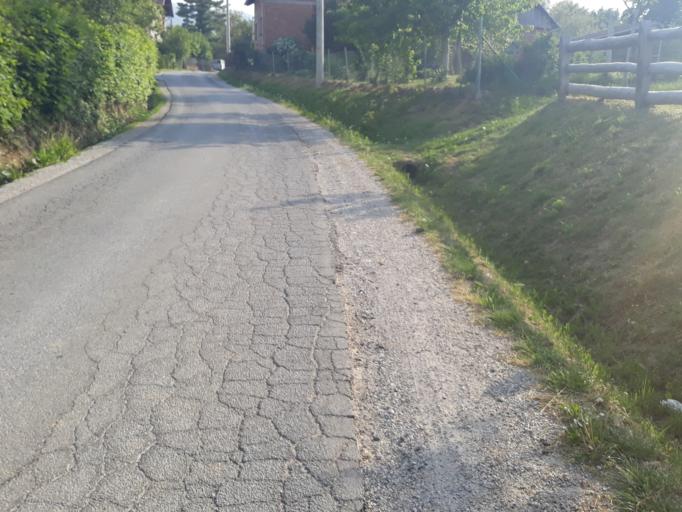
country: HR
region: Varazdinska
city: Ivanec
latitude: 46.2235
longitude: 16.1465
